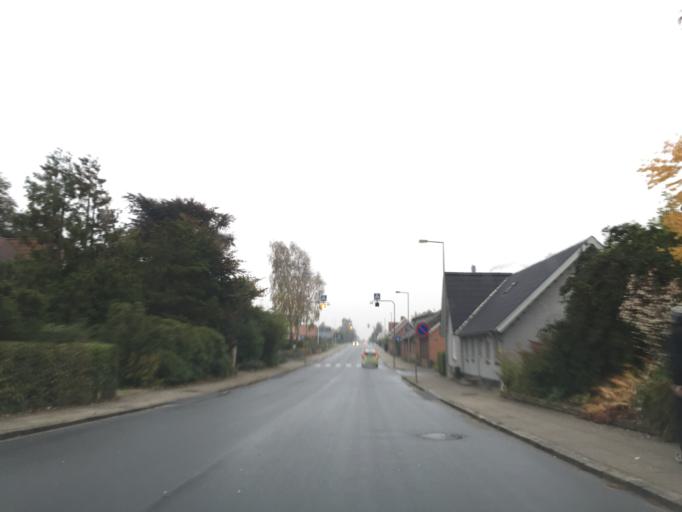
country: DK
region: Central Jutland
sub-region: Silkeborg Kommune
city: Kjellerup
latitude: 56.2853
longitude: 9.4320
